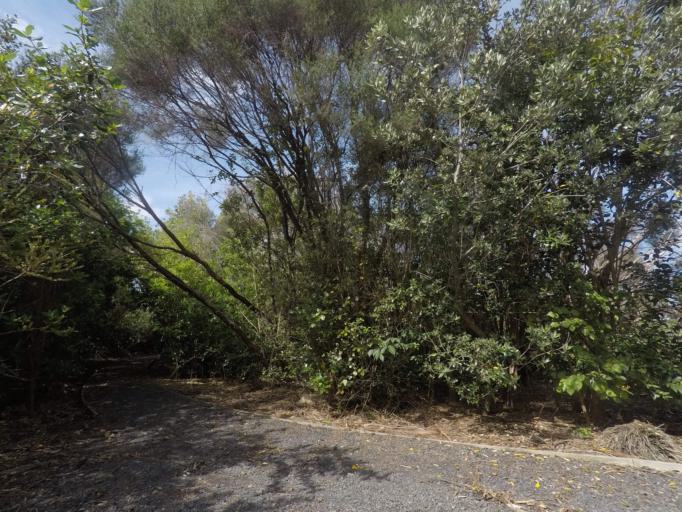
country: NZ
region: Auckland
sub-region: Auckland
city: Red Hill
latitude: -36.9871
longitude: 175.0377
